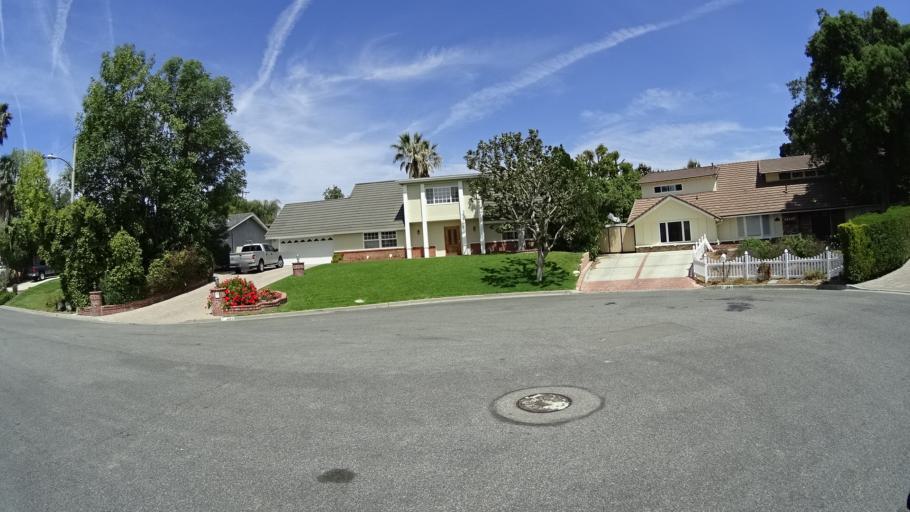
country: US
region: California
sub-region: Ventura County
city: Thousand Oaks
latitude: 34.2041
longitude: -118.8454
